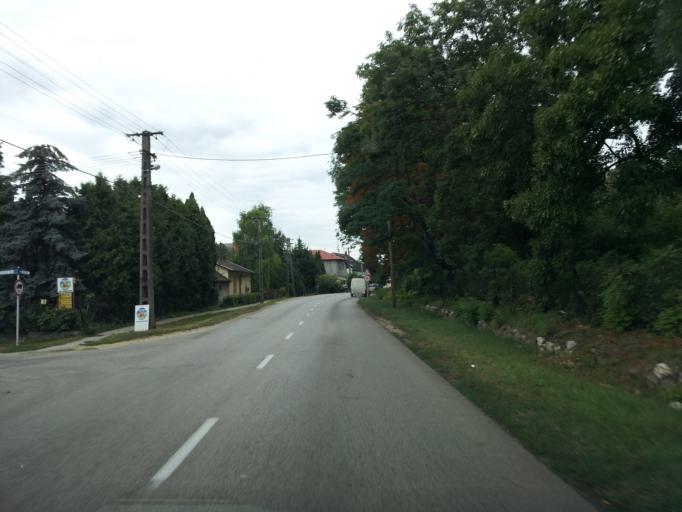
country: HU
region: Fejer
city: Velence
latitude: 47.2419
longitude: 18.6454
